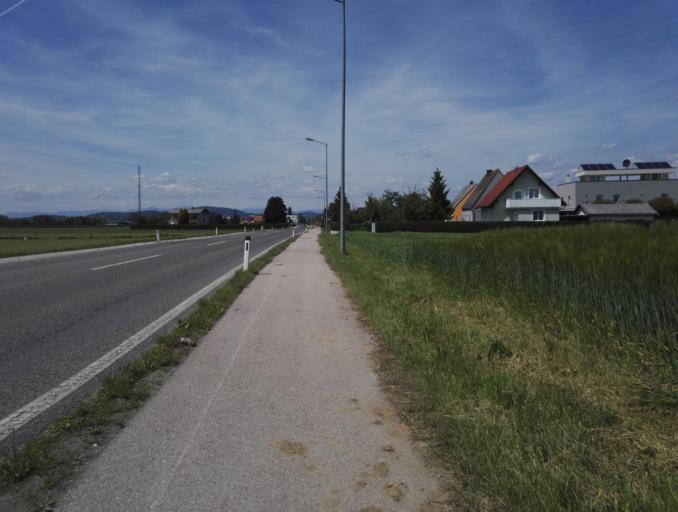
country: AT
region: Styria
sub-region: Politischer Bezirk Graz-Umgebung
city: Gossendorf
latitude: 46.9801
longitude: 15.4659
